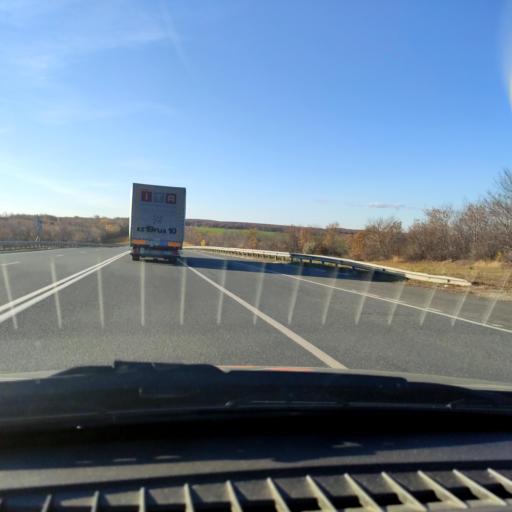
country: RU
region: Samara
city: Mezhdurechensk
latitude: 53.2565
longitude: 49.1250
